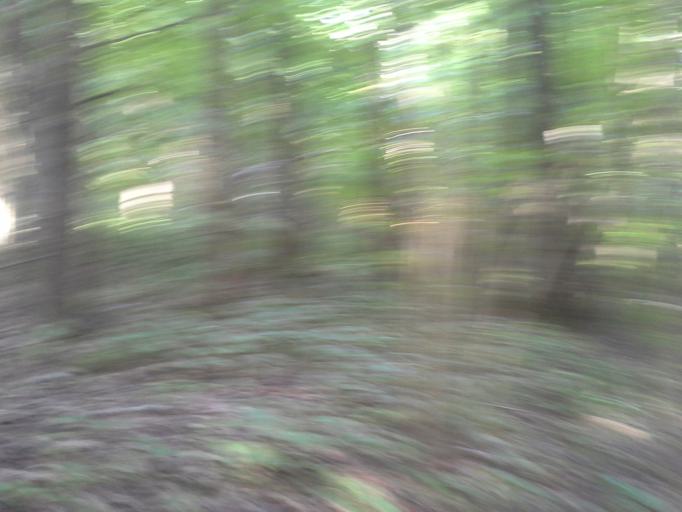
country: RU
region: Moskovskaya
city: Dubrovitsy
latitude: 55.4672
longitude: 37.4126
